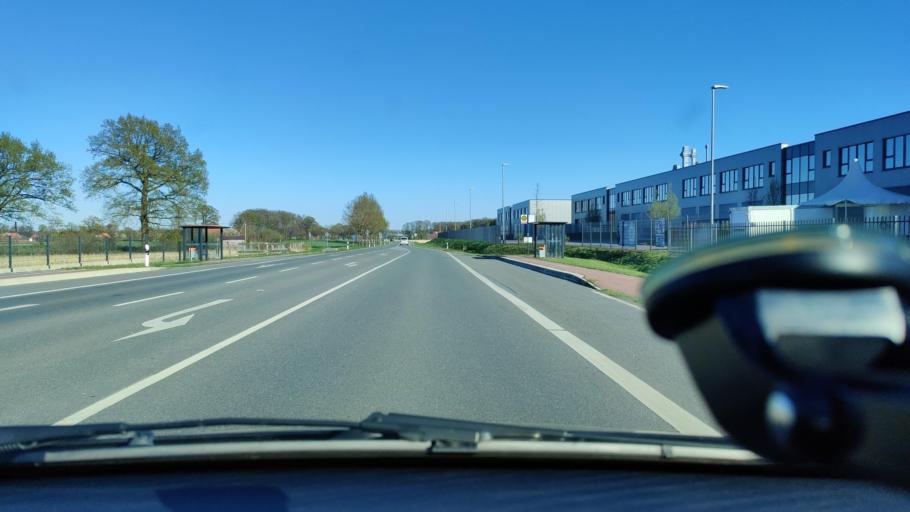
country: DE
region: North Rhine-Westphalia
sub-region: Regierungsbezirk Munster
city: Legden
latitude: 52.0502
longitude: 7.0647
